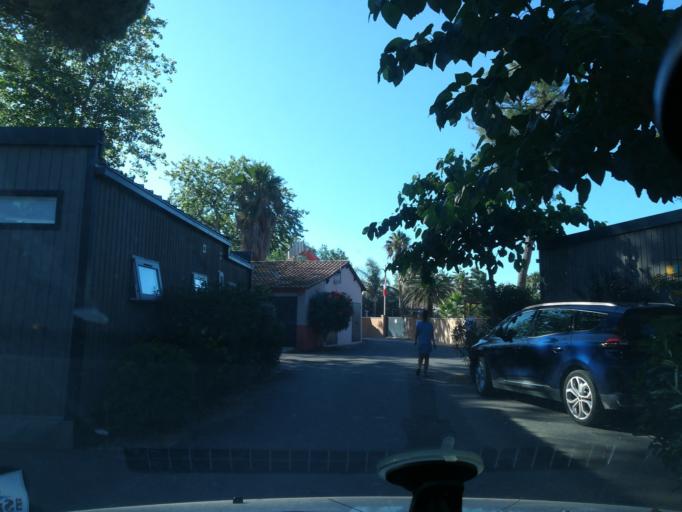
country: FR
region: Languedoc-Roussillon
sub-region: Departement de l'Herault
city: Portiragnes
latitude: 43.2814
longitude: 3.3642
